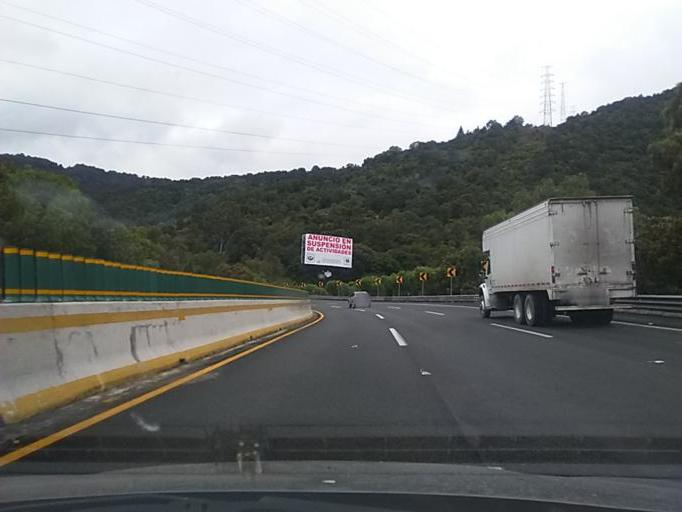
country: MX
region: Mexico City
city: Xochimilco
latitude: 19.2257
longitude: -99.1452
